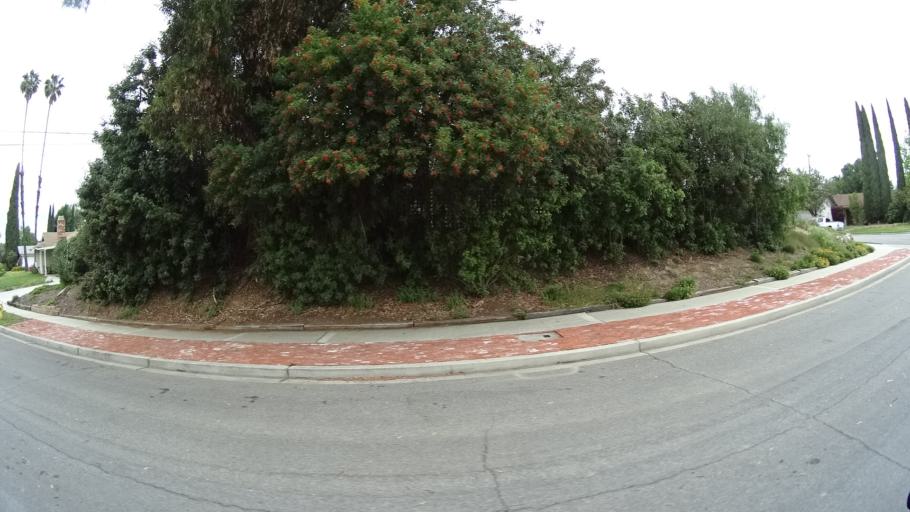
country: US
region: California
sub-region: Ventura County
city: Thousand Oaks
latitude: 34.2101
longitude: -118.8763
